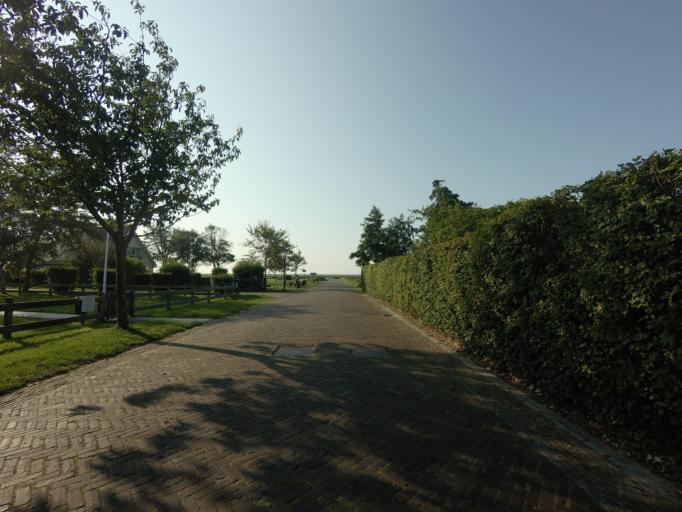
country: NL
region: Friesland
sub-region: Gemeente Schiermonnikoog
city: Schiermonnikoog
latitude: 53.4770
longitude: 6.1614
